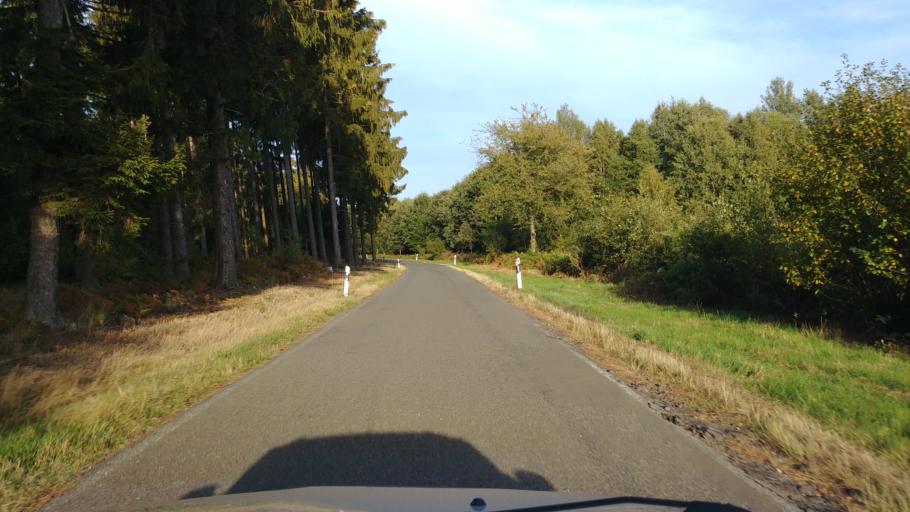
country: DE
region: Rheinland-Pfalz
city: Merschbach
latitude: 49.8179
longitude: 7.0185
